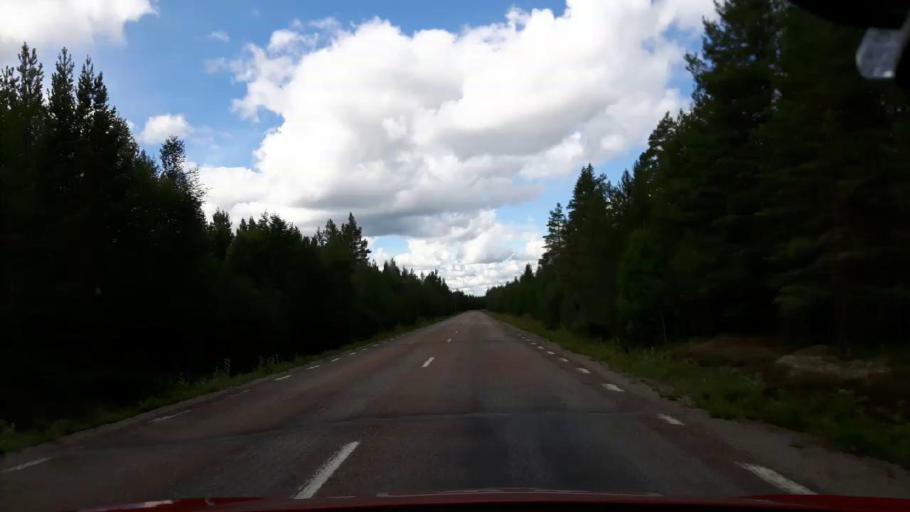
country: SE
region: Jaemtland
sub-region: Harjedalens Kommun
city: Sveg
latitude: 61.8393
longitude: 14.0041
